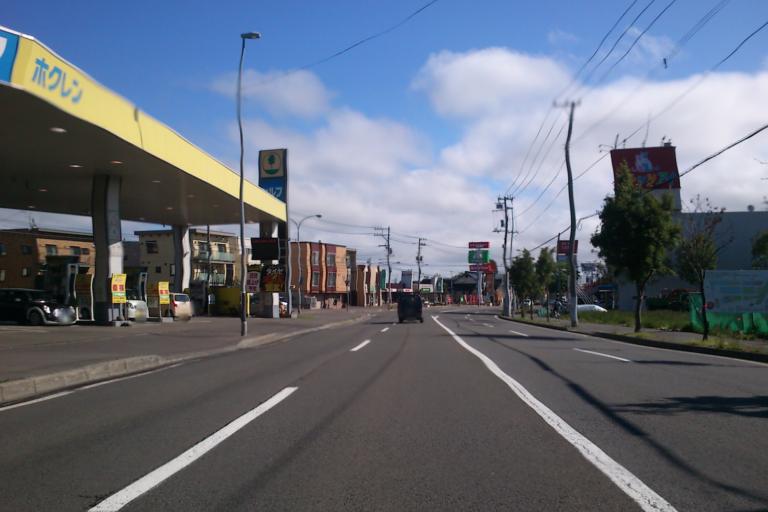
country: JP
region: Hokkaido
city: Sapporo
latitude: 43.1212
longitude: 141.2485
